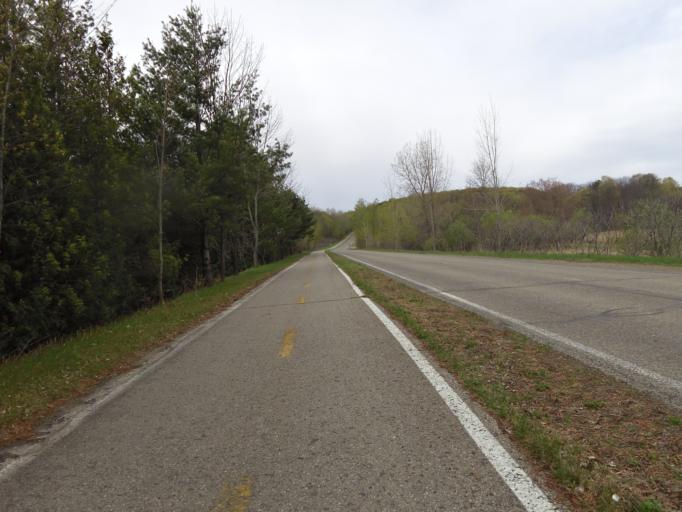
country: CA
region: Quebec
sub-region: Laurentides
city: Oka
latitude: 45.4827
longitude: -74.0324
